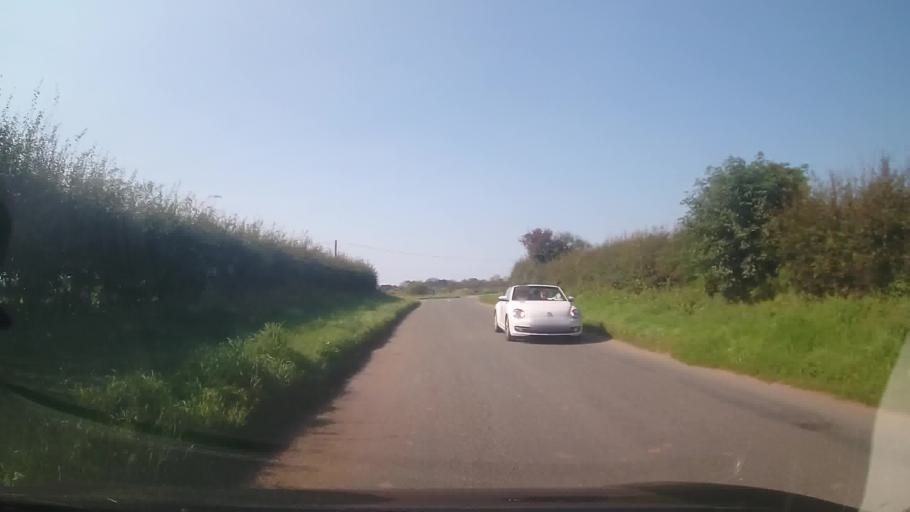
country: GB
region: Wales
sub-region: Pembrokeshire
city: Camrose
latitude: 51.8402
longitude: -4.9914
